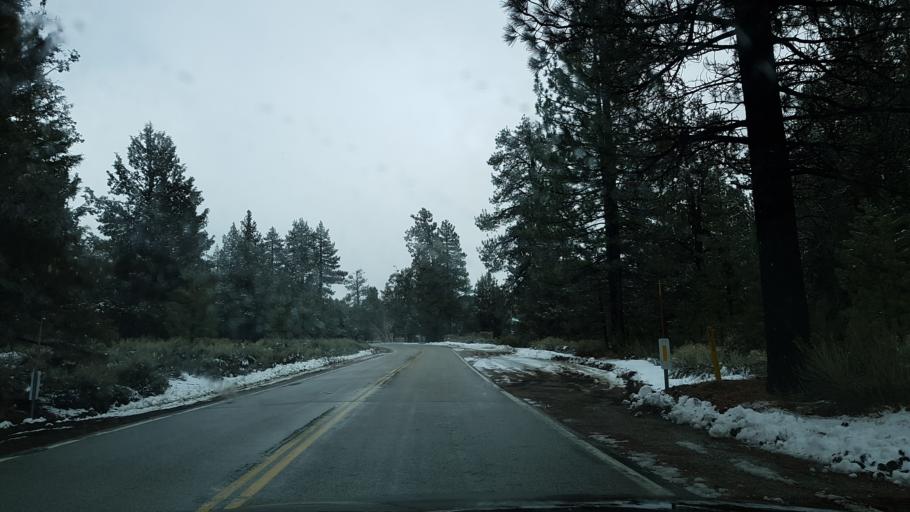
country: US
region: California
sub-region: San Bernardino County
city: Big Bear Lake
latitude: 34.2621
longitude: -116.9153
